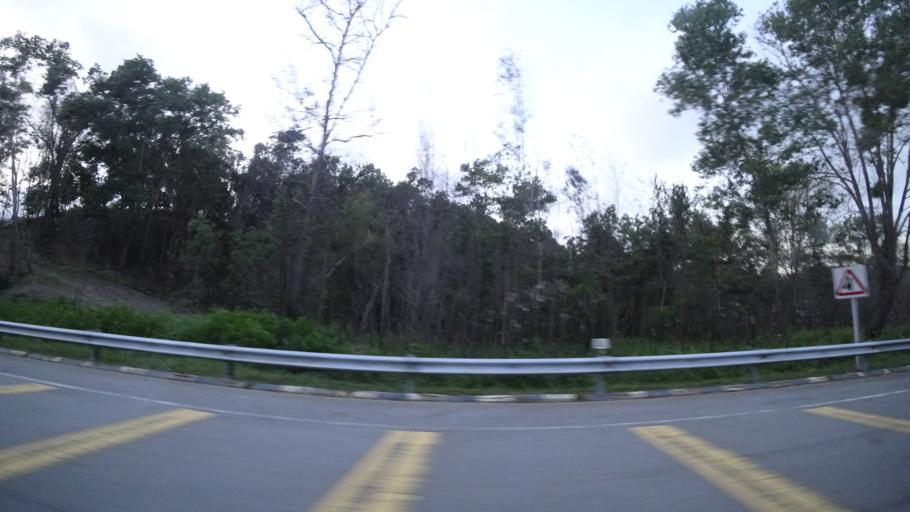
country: BN
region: Brunei and Muara
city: Bandar Seri Begawan
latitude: 4.9064
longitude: 114.7993
